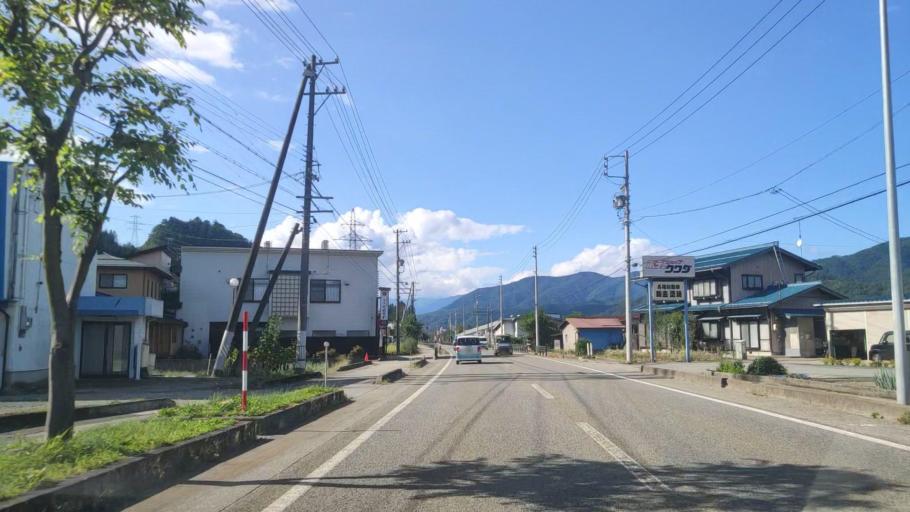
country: JP
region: Gifu
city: Takayama
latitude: 36.2362
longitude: 137.1772
